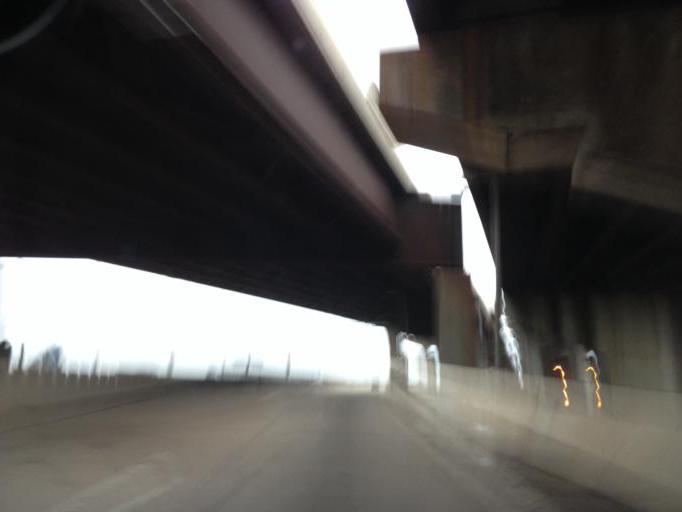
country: US
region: Maryland
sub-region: Baltimore County
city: Dundalk
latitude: 39.2730
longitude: -76.5542
